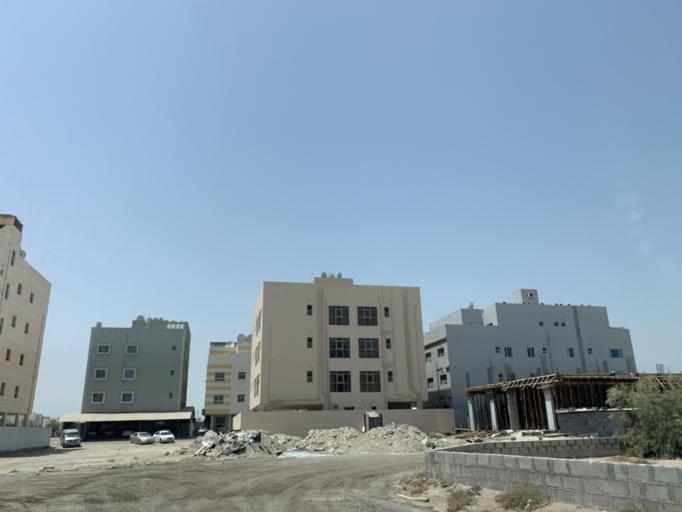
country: BH
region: Northern
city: Madinat `Isa
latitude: 26.1917
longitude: 50.5471
